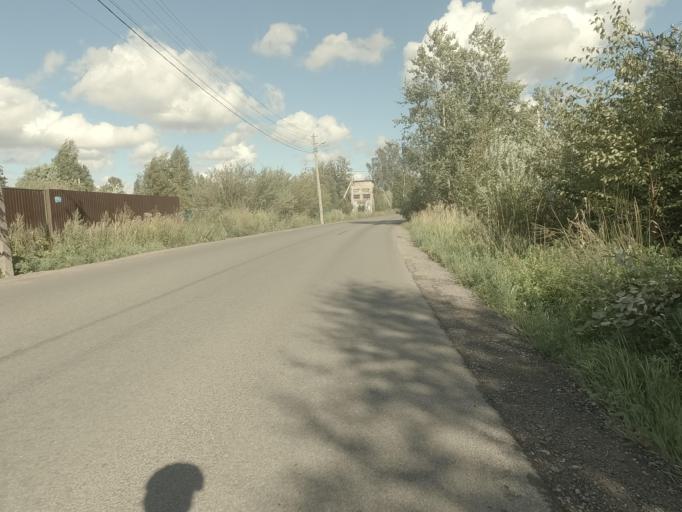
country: RU
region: Leningrad
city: Yanino Vtoroye
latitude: 59.9793
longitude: 30.5659
